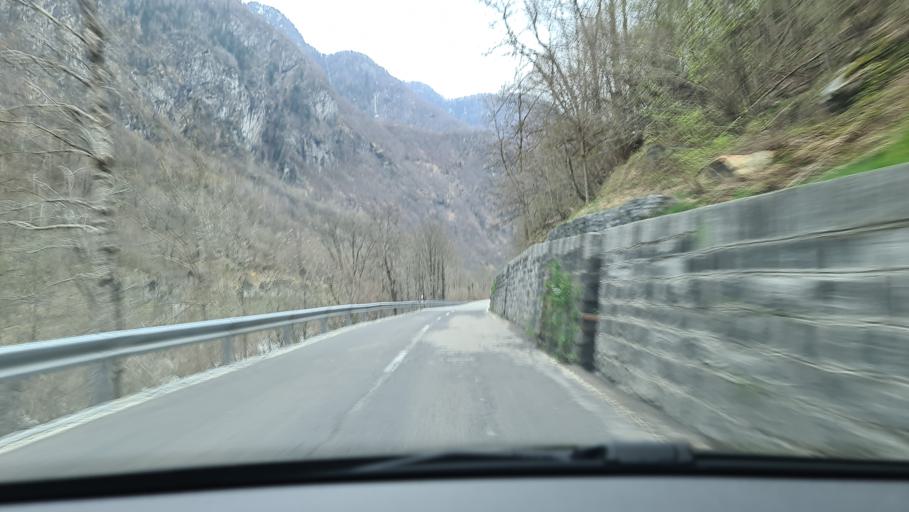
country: CH
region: Ticino
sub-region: Vallemaggia District
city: Cevio
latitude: 46.3679
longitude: 8.6559
